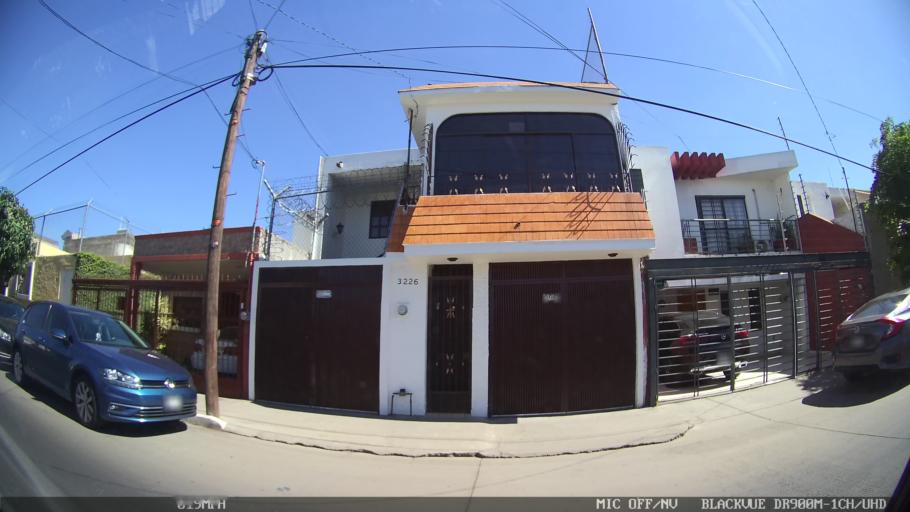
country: MX
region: Jalisco
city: Tlaquepaque
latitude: 20.6550
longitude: -103.2927
